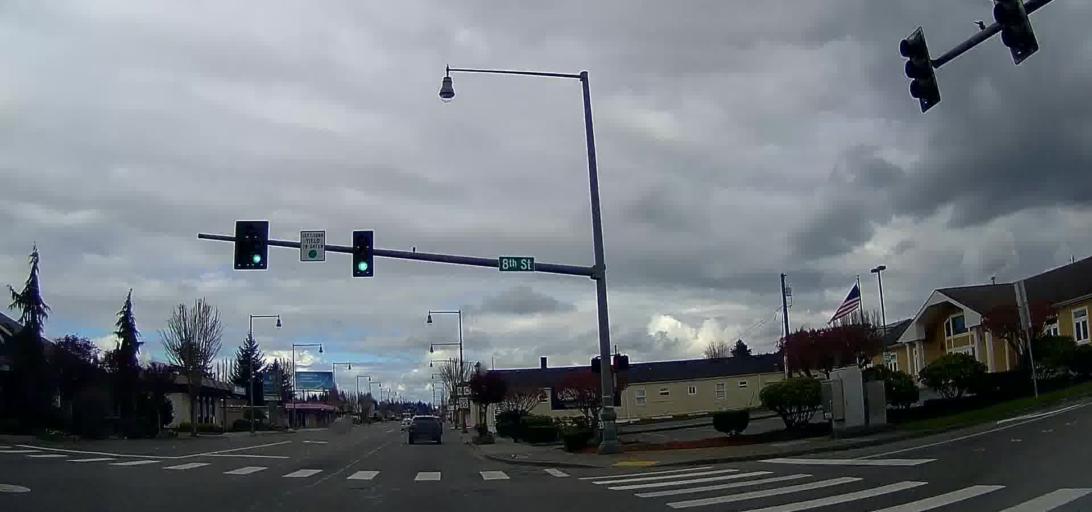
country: US
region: Washington
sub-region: Snohomish County
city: Marysville
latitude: 48.0554
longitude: -122.1768
